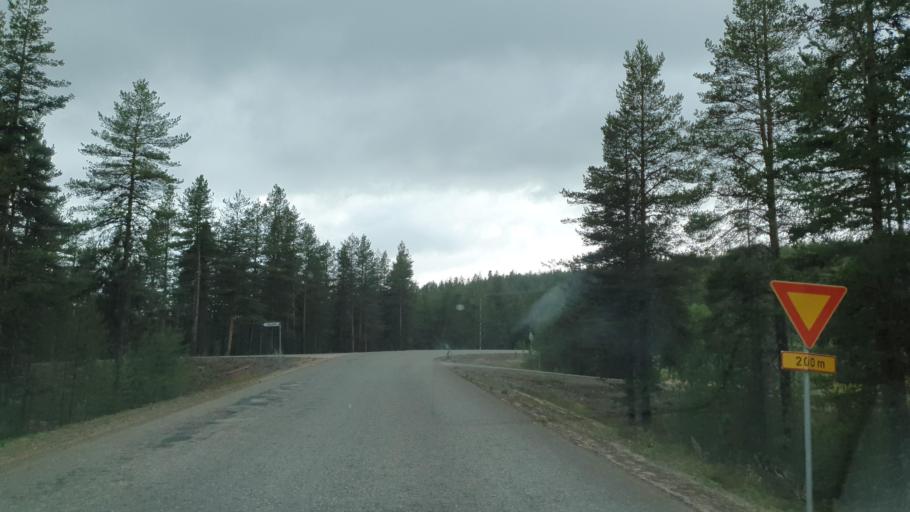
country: FI
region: Lapland
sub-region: Tunturi-Lappi
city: Kolari
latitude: 67.5388
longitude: 23.9497
